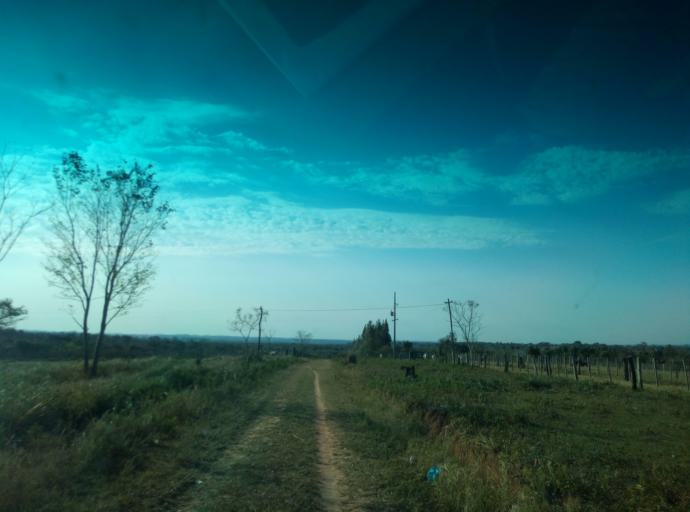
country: PY
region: Caaguazu
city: Doctor Cecilio Baez
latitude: -25.1626
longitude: -56.2321
